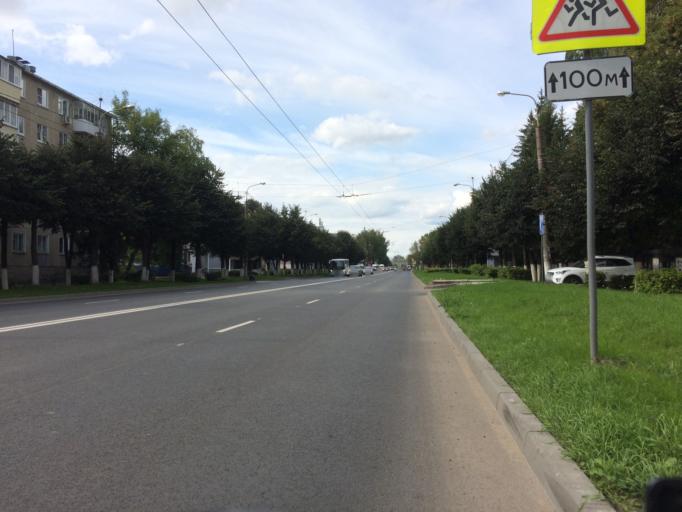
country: RU
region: Mariy-El
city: Yoshkar-Ola
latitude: 56.6351
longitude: 47.8761
